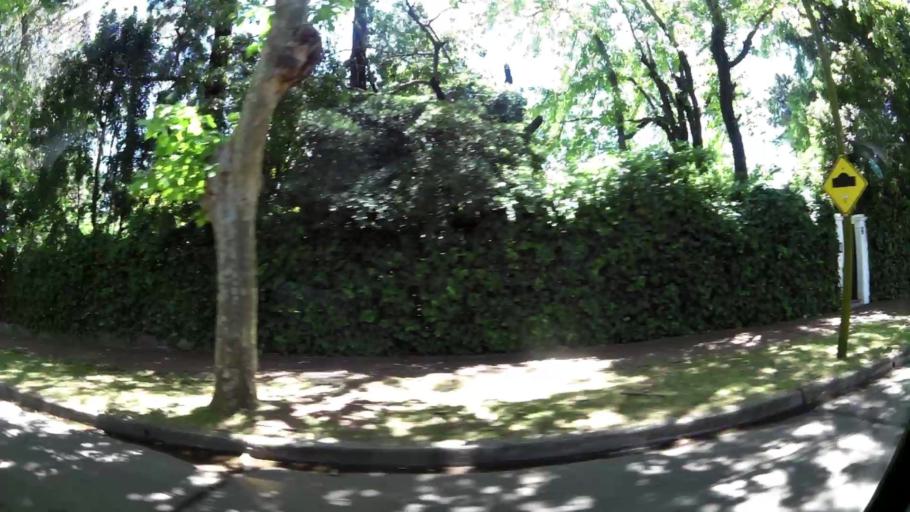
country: AR
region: Buenos Aires
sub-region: Partido de Vicente Lopez
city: Olivos
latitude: -34.4883
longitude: -58.4888
